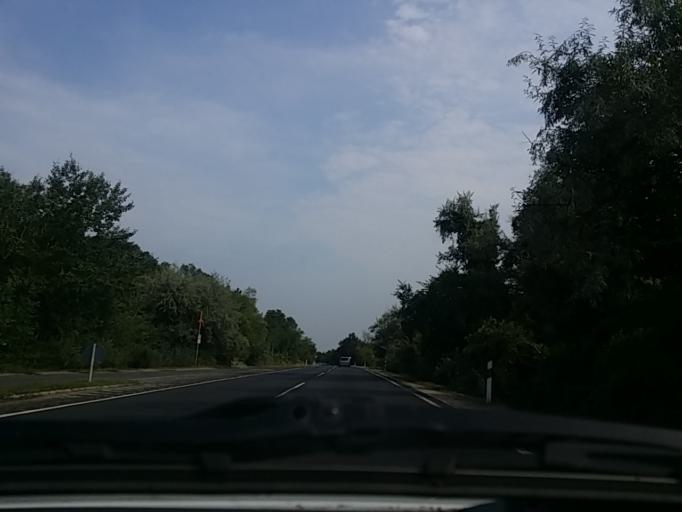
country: HU
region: Fejer
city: Szarliget
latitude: 47.4890
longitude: 18.5254
